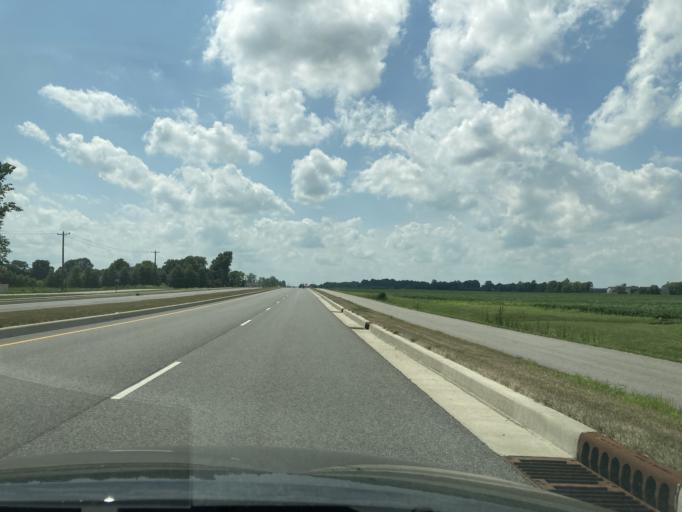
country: US
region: Indiana
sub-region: Hamilton County
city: Carmel
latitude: 39.9996
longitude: -86.1920
